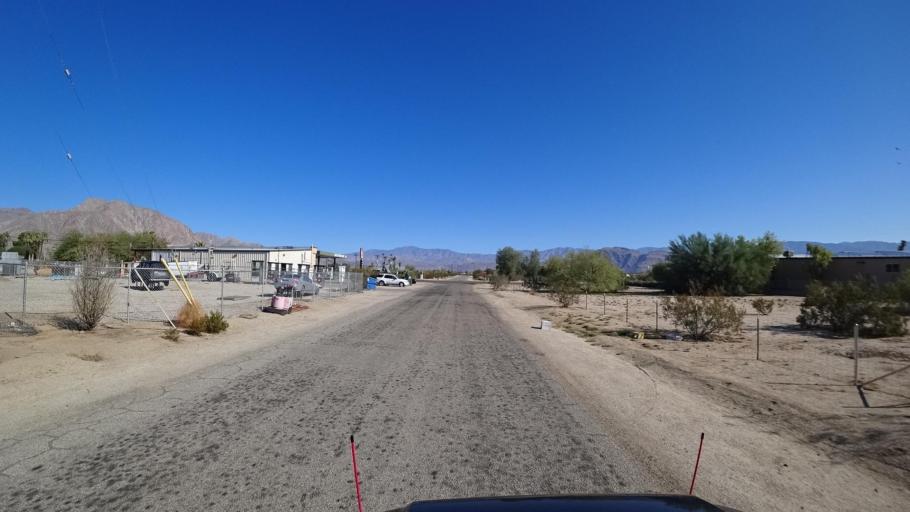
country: US
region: California
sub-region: San Diego County
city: Borrego Springs
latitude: 33.2557
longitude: -116.3724
